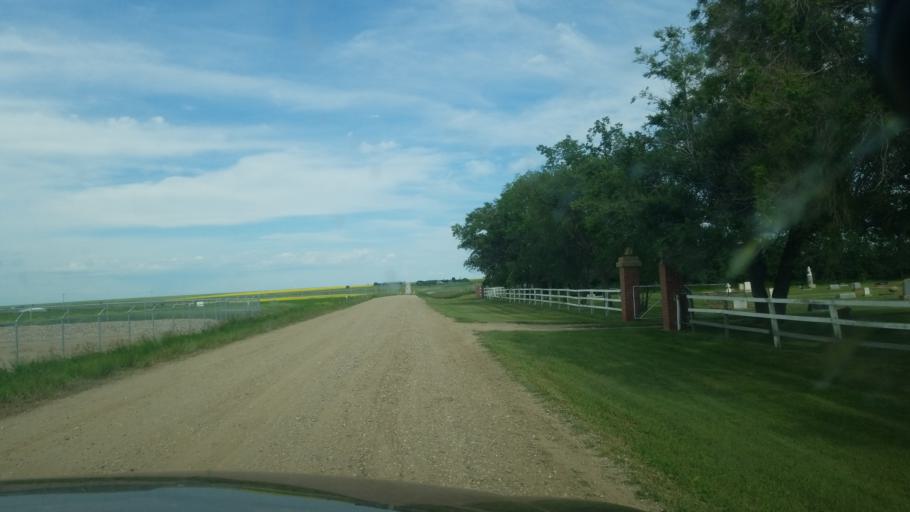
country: CA
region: Saskatchewan
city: Outlook
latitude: 51.4747
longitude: -107.5165
